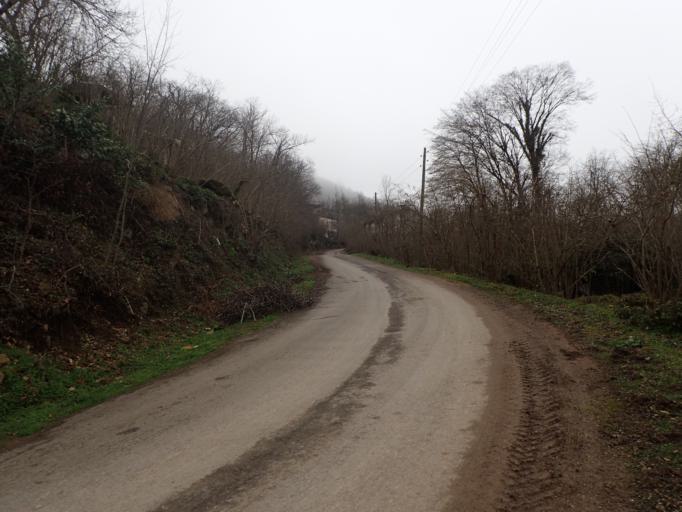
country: TR
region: Ordu
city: Camas
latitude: 40.9283
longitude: 37.5517
